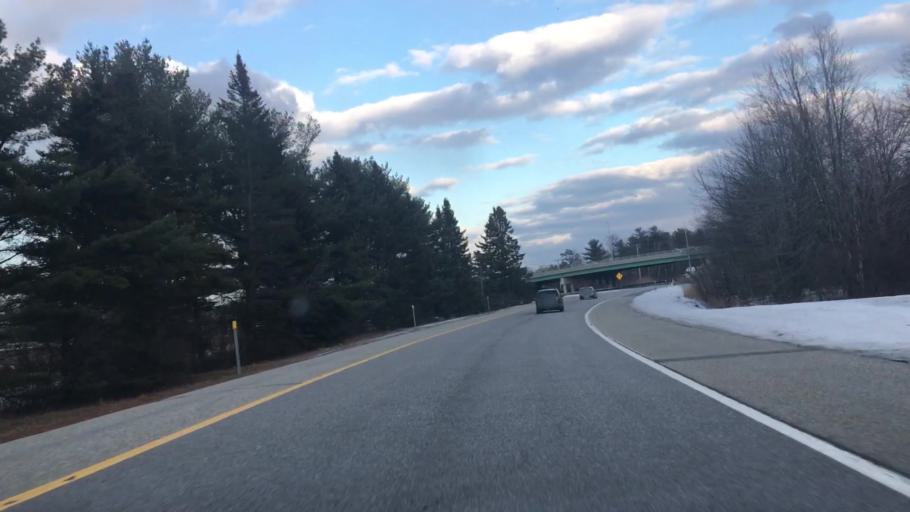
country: US
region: Maine
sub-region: Cumberland County
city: South Portland Gardens
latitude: 43.6308
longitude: -70.3437
